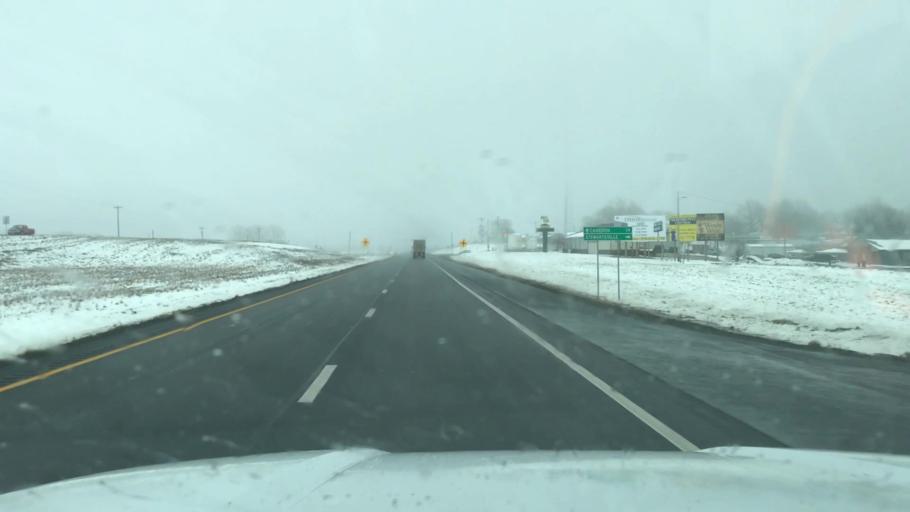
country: US
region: Missouri
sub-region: Clinton County
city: Gower
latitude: 39.7620
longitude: -94.5014
